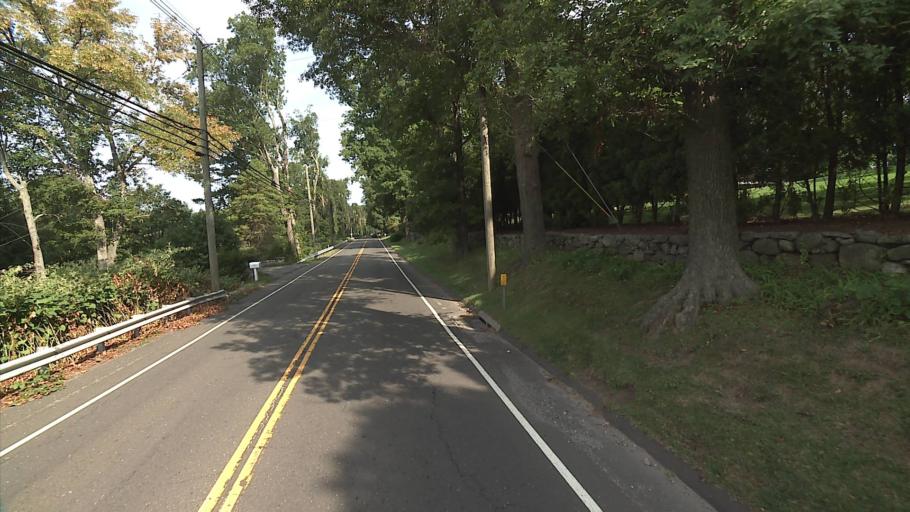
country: US
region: Connecticut
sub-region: Fairfield County
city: New Canaan
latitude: 41.1751
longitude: -73.4972
